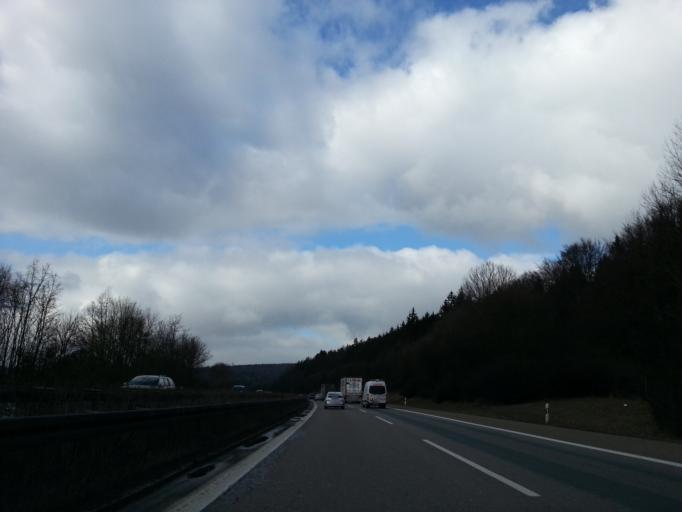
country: DE
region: Bavaria
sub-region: Upper Palatinate
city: Velburg
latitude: 49.1944
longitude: 11.6818
